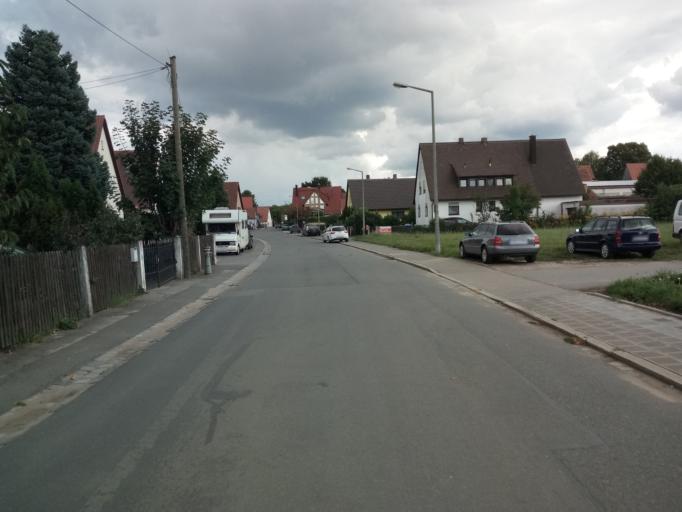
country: DE
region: Bavaria
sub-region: Regierungsbezirk Mittelfranken
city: Wetzendorf
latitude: 49.4880
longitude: 11.0703
